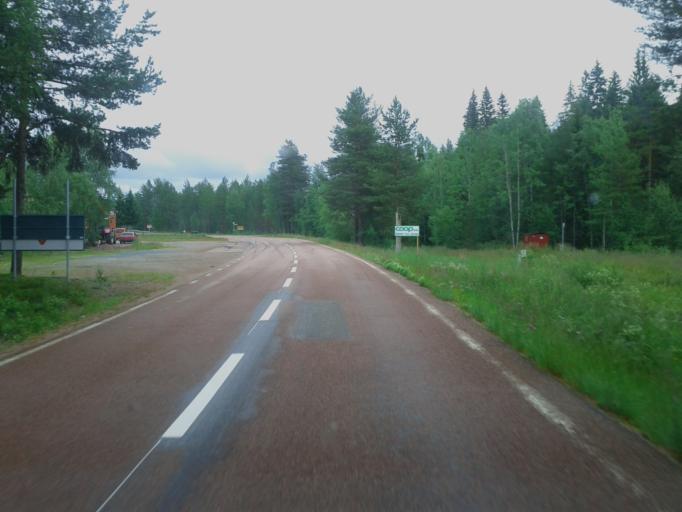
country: NO
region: Hedmark
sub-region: Trysil
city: Innbygda
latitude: 61.8515
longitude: 12.7080
